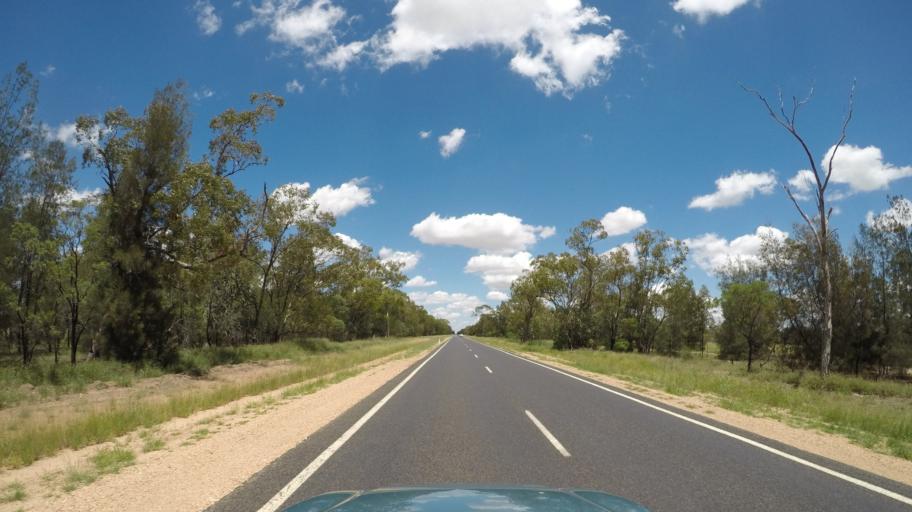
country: AU
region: Queensland
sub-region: Goondiwindi
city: Goondiwindi
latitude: -28.1620
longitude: 150.6231
